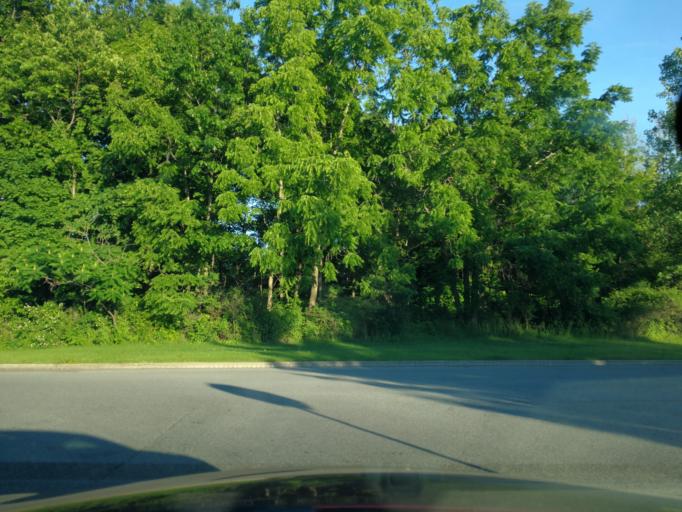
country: US
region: New York
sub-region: Monroe County
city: Greece
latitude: 43.2044
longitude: -77.6732
